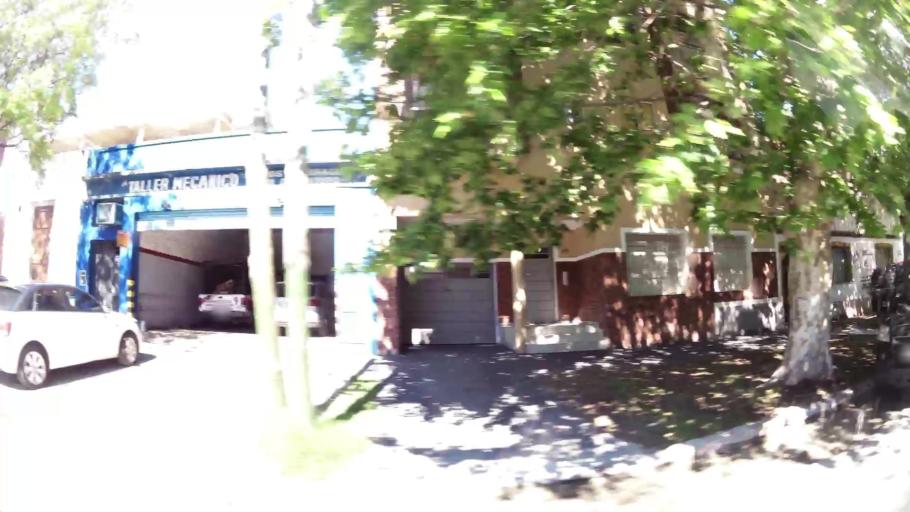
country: AR
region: Buenos Aires
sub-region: Partido de Lomas de Zamora
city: Lomas de Zamora
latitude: -34.7579
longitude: -58.4081
